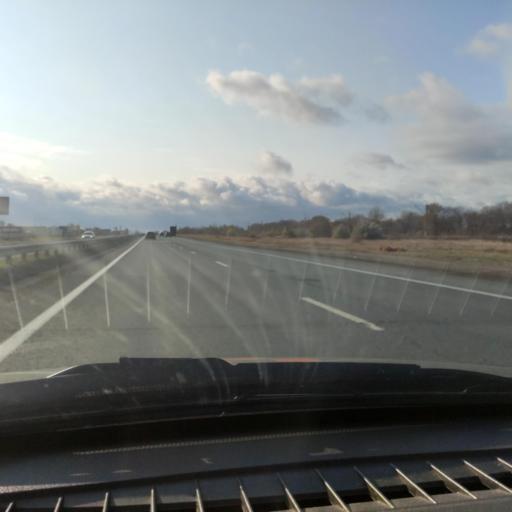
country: RU
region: Samara
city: Tol'yatti
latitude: 53.5690
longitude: 49.3792
